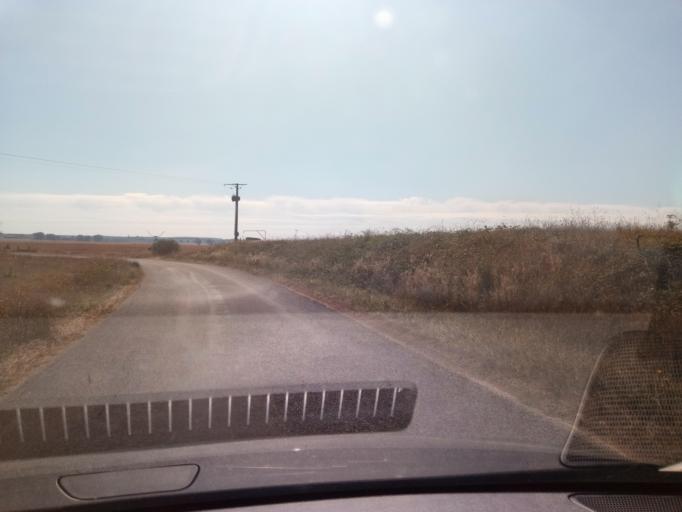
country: FR
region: Poitou-Charentes
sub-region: Departement de la Vienne
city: Lussac-les-Chateaux
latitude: 46.3828
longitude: 0.7811
